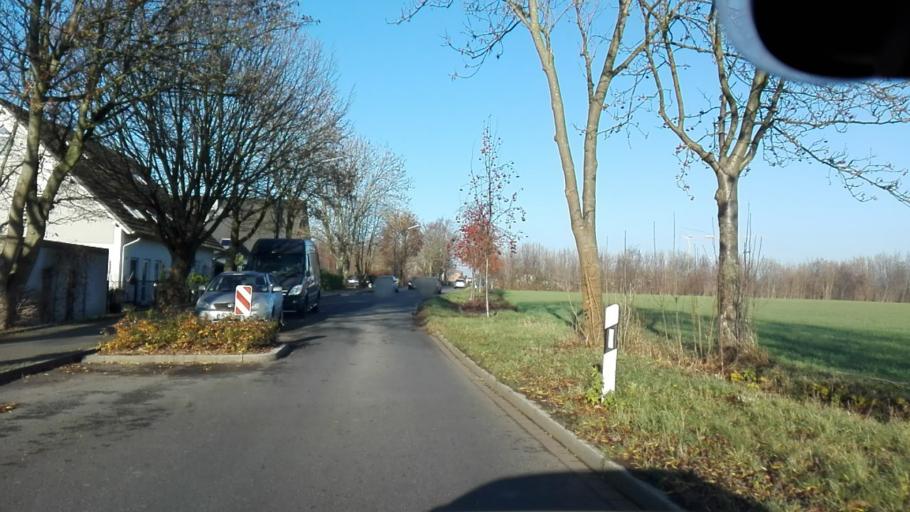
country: DE
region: North Rhine-Westphalia
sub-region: Regierungsbezirk Arnsberg
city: Holzwickede
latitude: 51.5137
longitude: 7.6284
